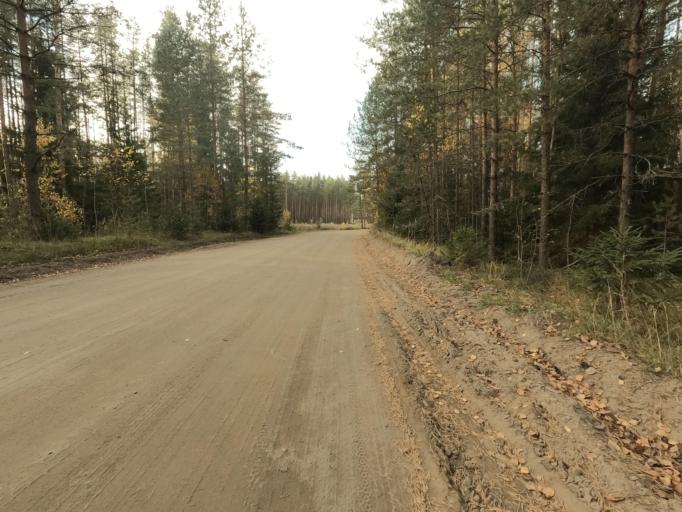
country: RU
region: Leningrad
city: Priladozhskiy
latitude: 59.6313
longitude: 31.3909
